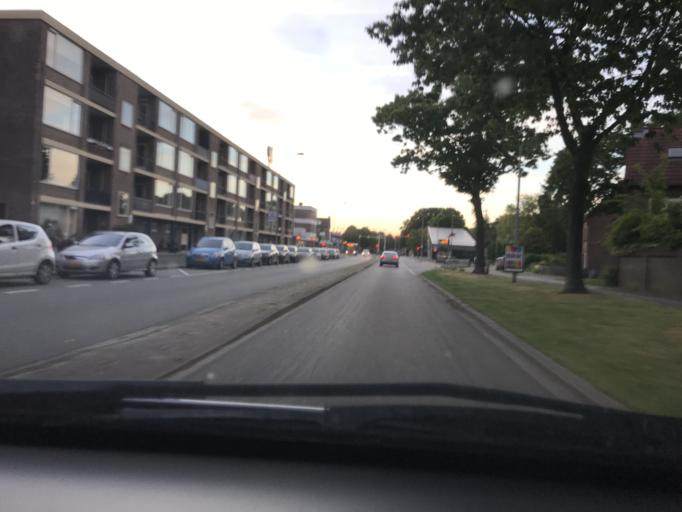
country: NL
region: North Brabant
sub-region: Gemeente Breda
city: Breda
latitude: 51.5689
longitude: 4.7937
